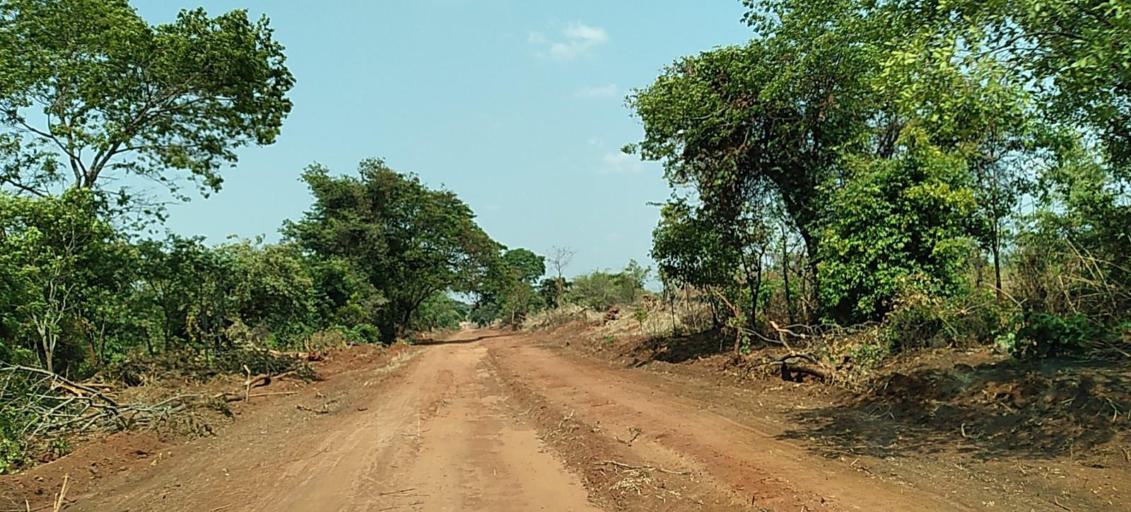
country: ZM
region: Copperbelt
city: Luanshya
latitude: -13.0903
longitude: 28.2758
